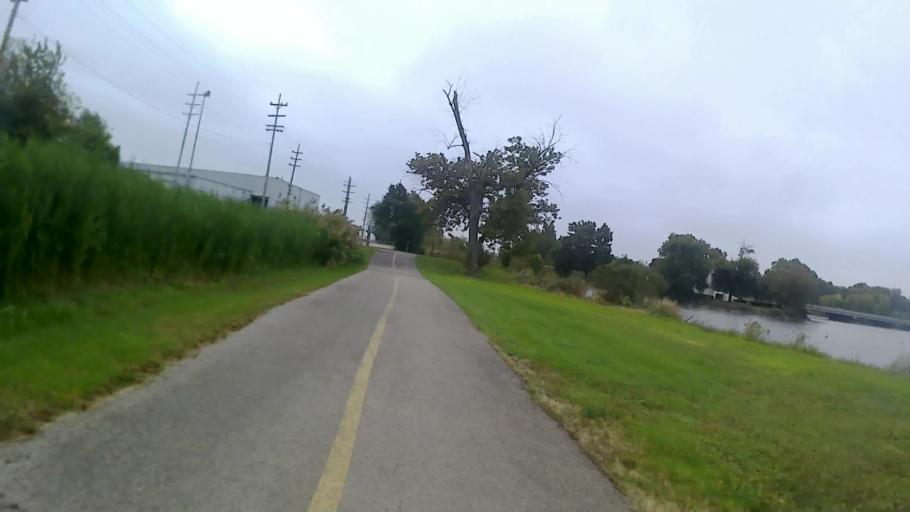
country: US
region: Illinois
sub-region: Kane County
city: Aurora
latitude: 41.7726
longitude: -88.3084
